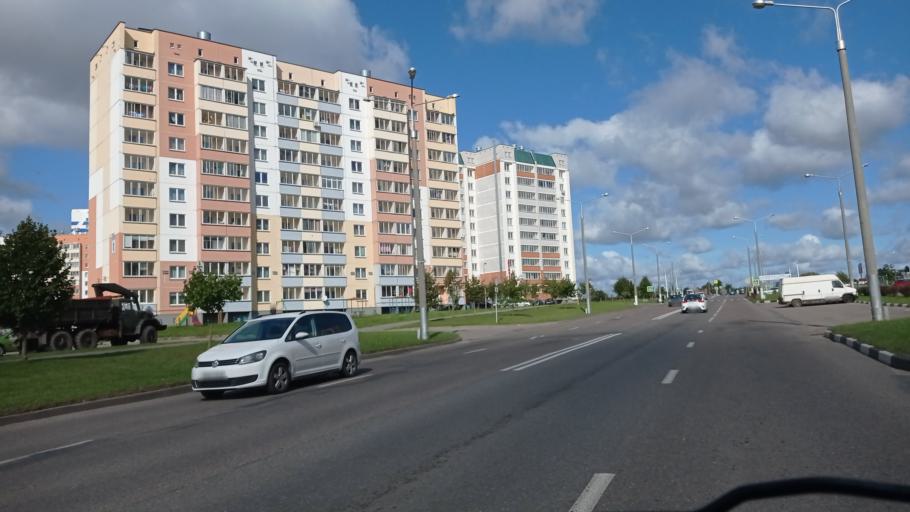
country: BY
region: Vitebsk
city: Vitebsk
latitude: 55.1715
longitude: 30.2576
